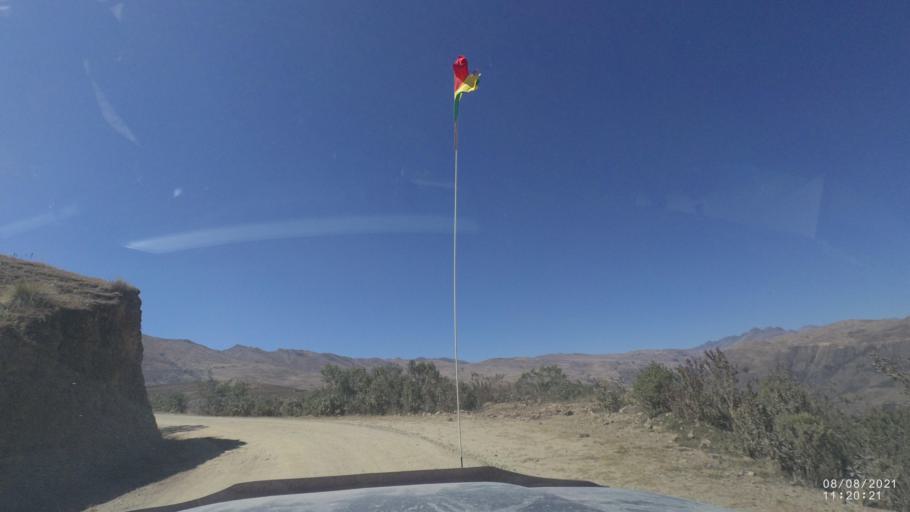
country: BO
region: Cochabamba
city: Colchani
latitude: -16.7802
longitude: -66.6606
